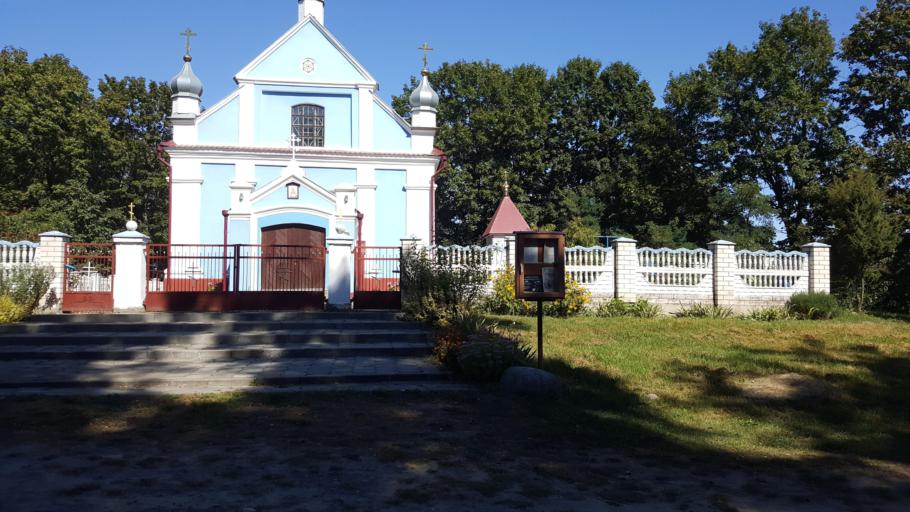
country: BY
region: Brest
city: Vysokaye
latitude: 52.2359
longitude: 23.4927
